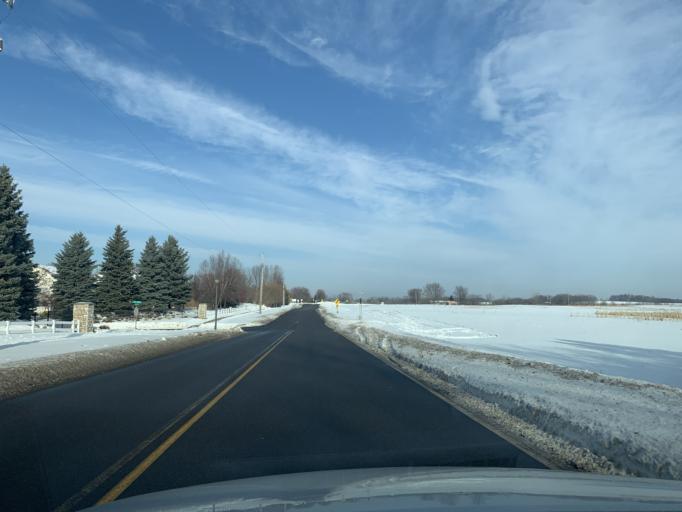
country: US
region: Minnesota
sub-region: Wright County
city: Albertville
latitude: 45.2205
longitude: -93.6441
